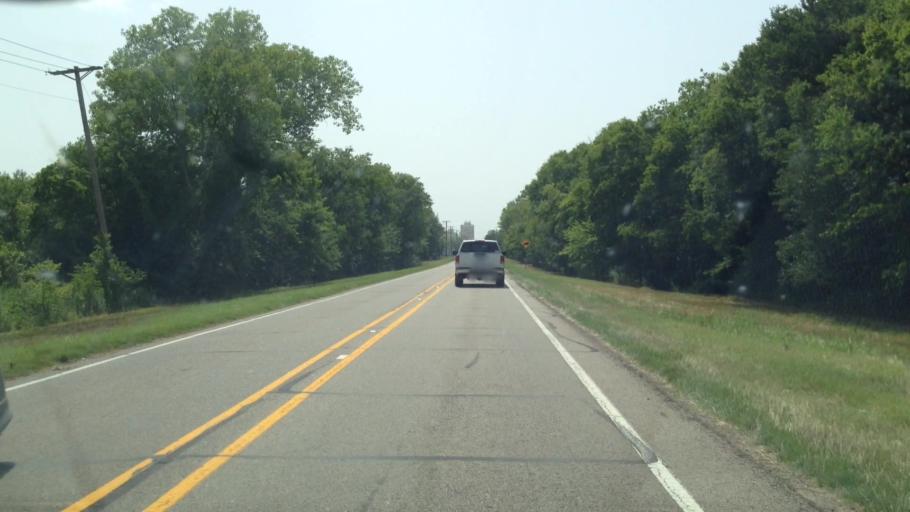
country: US
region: Texas
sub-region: Hunt County
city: Greenville
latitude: 33.1397
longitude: -96.0942
